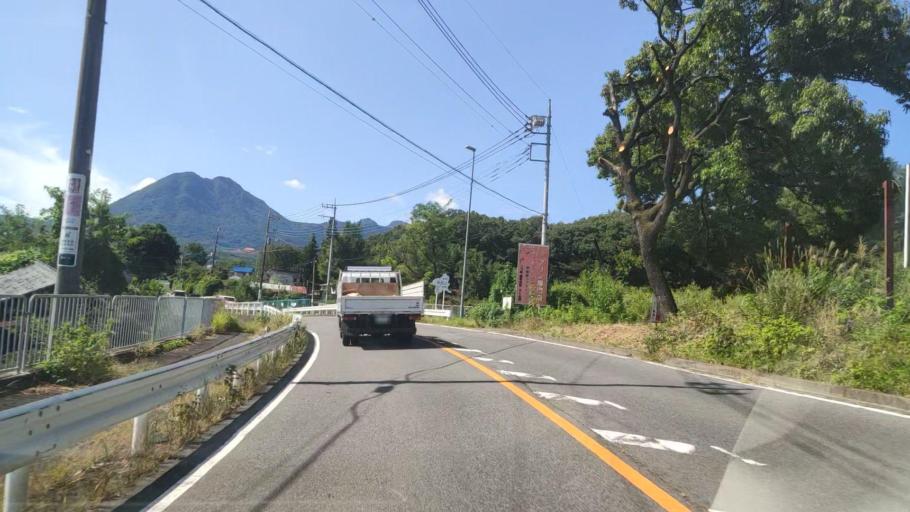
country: JP
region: Gunma
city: Shibukawa
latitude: 36.5028
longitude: 138.9658
